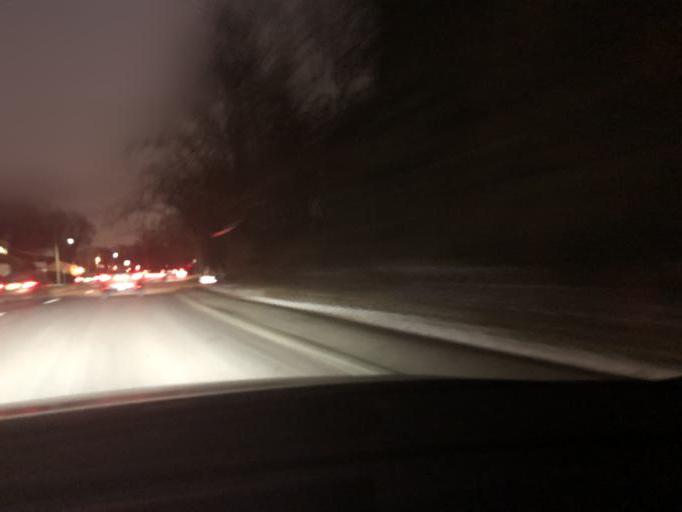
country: US
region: New Jersey
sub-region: Essex County
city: South Orange
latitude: 40.7705
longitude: -74.2749
